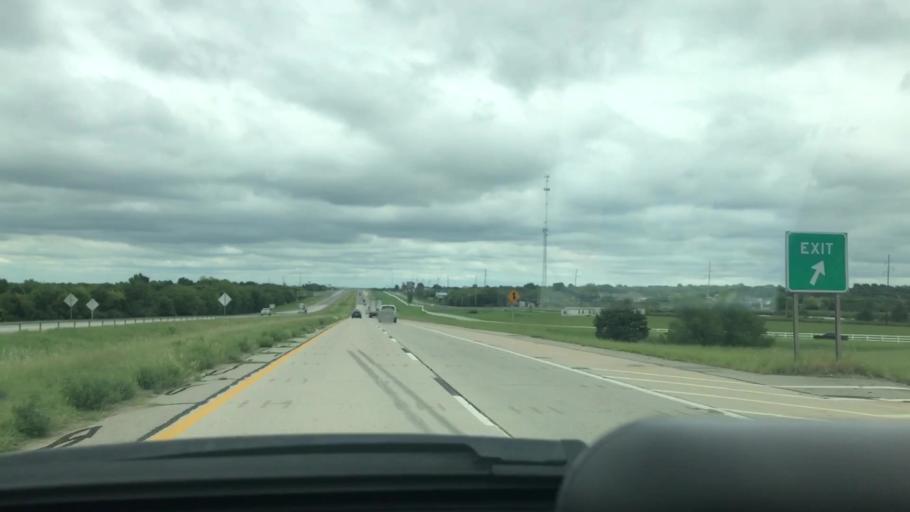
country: US
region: Oklahoma
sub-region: McIntosh County
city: Checotah
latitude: 35.4598
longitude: -95.5433
